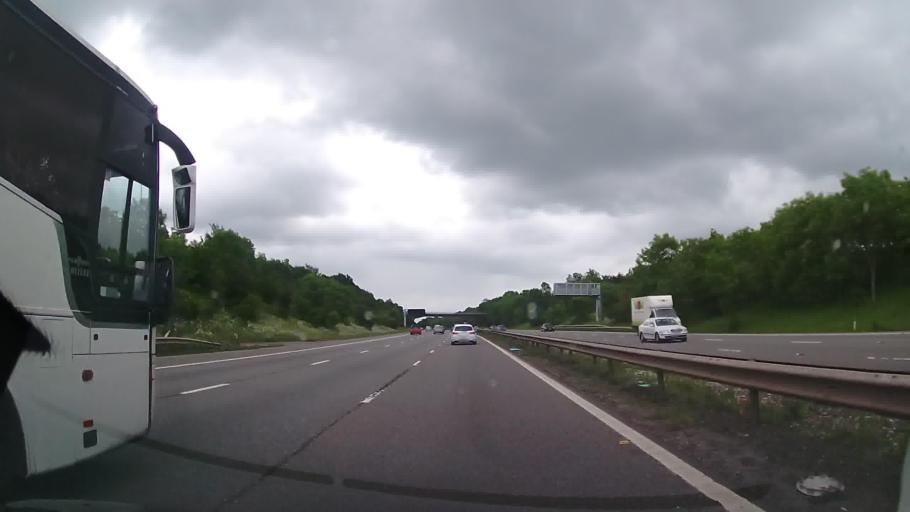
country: GB
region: England
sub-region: Leicestershire
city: Markfield
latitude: 52.6750
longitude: -1.2856
